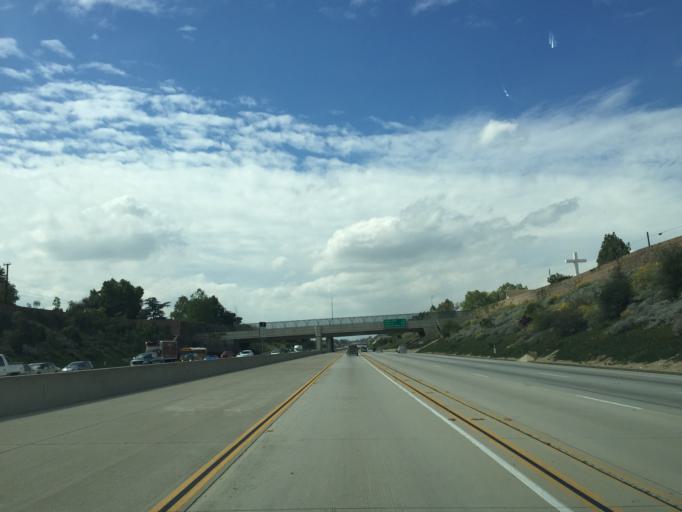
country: US
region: California
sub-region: Los Angeles County
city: Claremont
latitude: 34.1202
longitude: -117.7177
